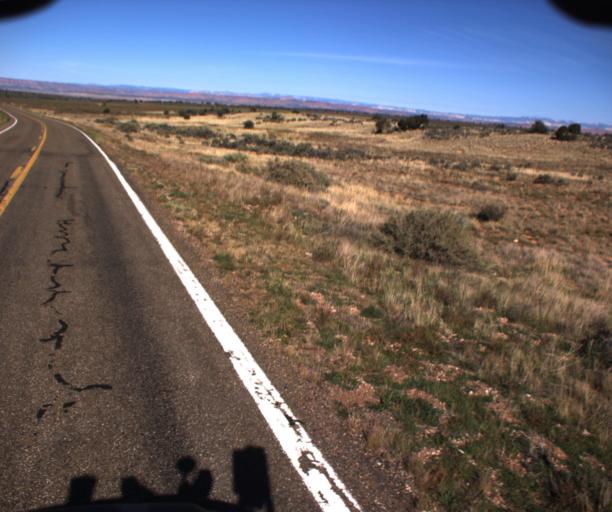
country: US
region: Arizona
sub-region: Coconino County
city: Fredonia
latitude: 36.8502
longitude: -112.2881
